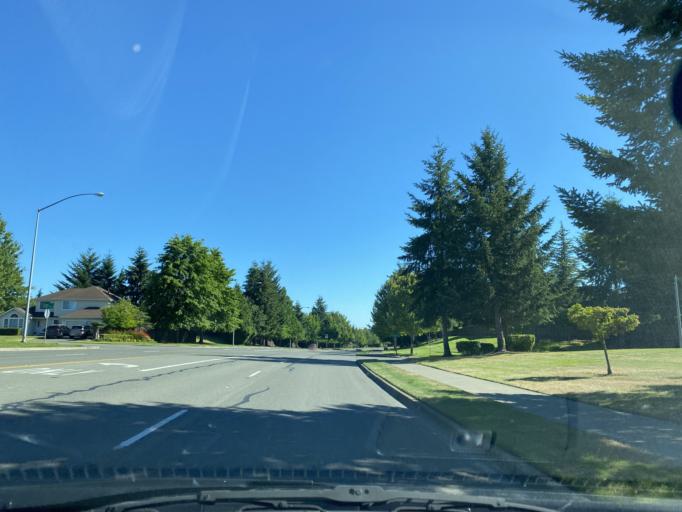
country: US
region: Washington
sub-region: Pierce County
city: McMillin
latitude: 47.1080
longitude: -122.2503
